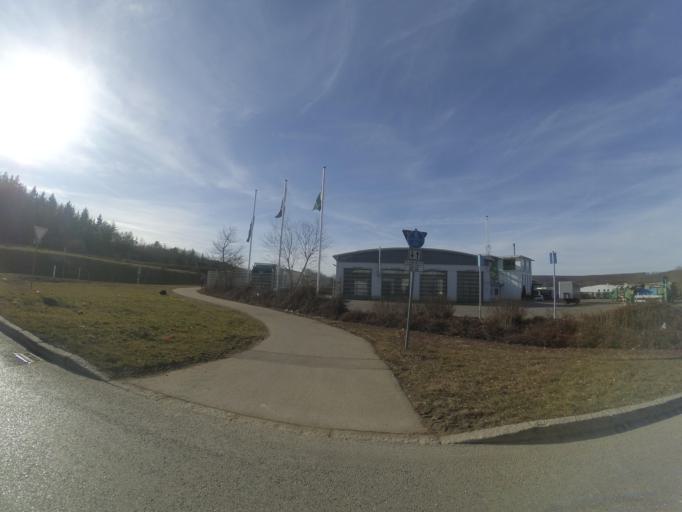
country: DE
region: Baden-Wuerttemberg
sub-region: Regierungsbezirk Stuttgart
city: Herbrechtingen
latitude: 48.6261
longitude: 10.2045
